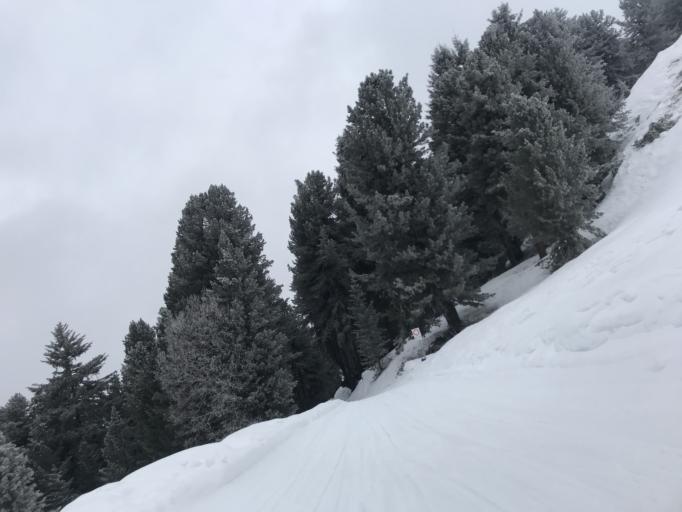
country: IT
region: Trentino-Alto Adige
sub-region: Bolzano
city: San Pietro
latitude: 46.6847
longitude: 11.7087
